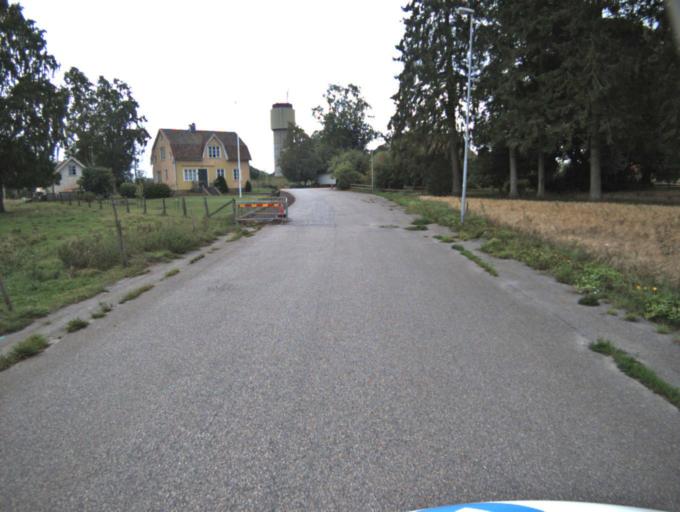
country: SE
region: Vaestra Goetaland
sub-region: Falkopings Kommun
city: Falkoeping
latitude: 57.9890
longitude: 13.5364
